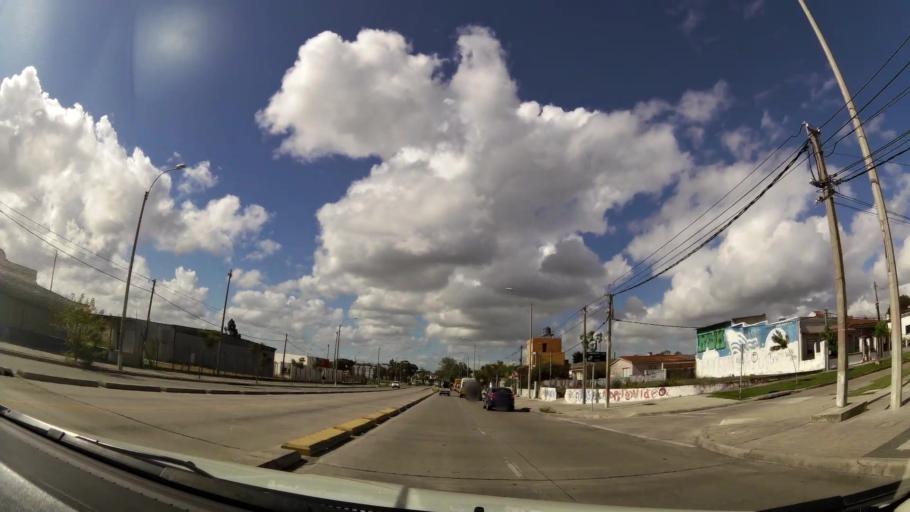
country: UY
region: Canelones
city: La Paz
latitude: -34.8291
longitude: -56.2203
